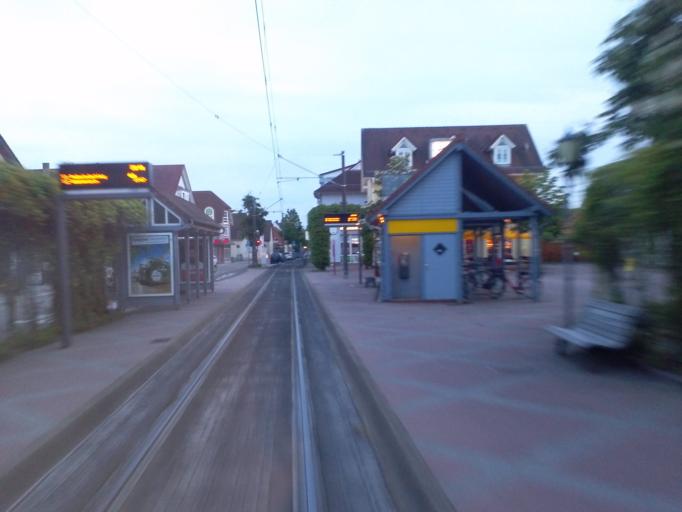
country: DE
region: Baden-Wuerttemberg
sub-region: Karlsruhe Region
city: Rheinstetten
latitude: 48.9749
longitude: 8.3123
